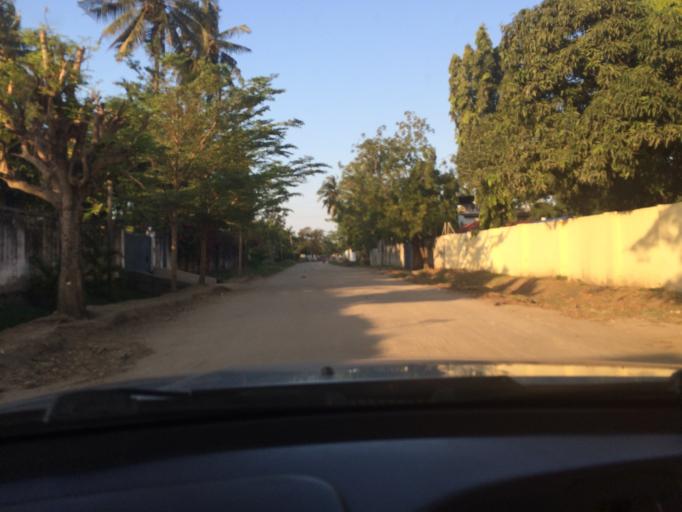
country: TZ
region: Dar es Salaam
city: Magomeni
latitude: -6.7751
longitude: 39.2555
